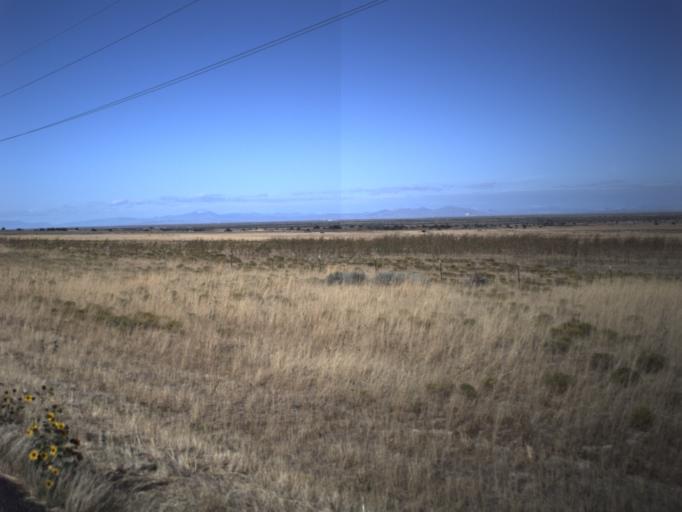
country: US
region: Utah
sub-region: Millard County
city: Delta
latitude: 39.4625
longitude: -112.2868
